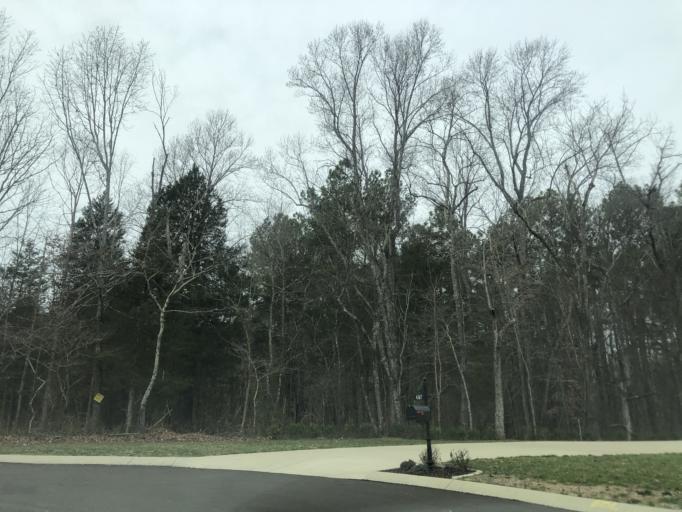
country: US
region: Tennessee
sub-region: Robertson County
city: Greenbrier
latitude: 36.4009
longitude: -86.8231
